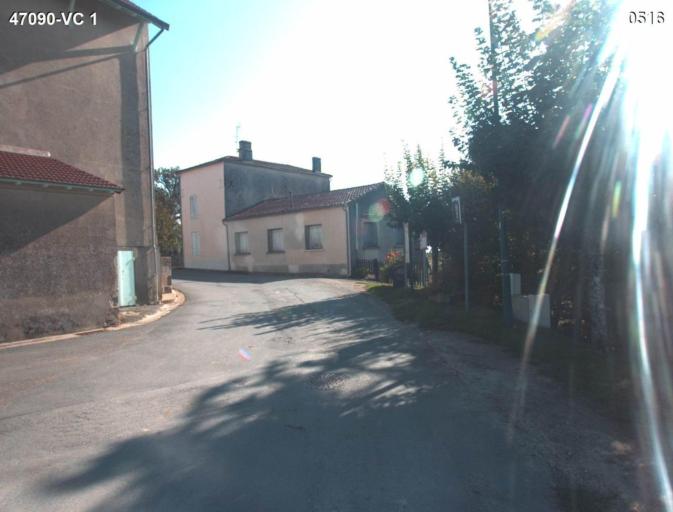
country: FR
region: Aquitaine
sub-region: Departement du Lot-et-Garonne
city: Nerac
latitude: 44.1681
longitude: 0.3780
